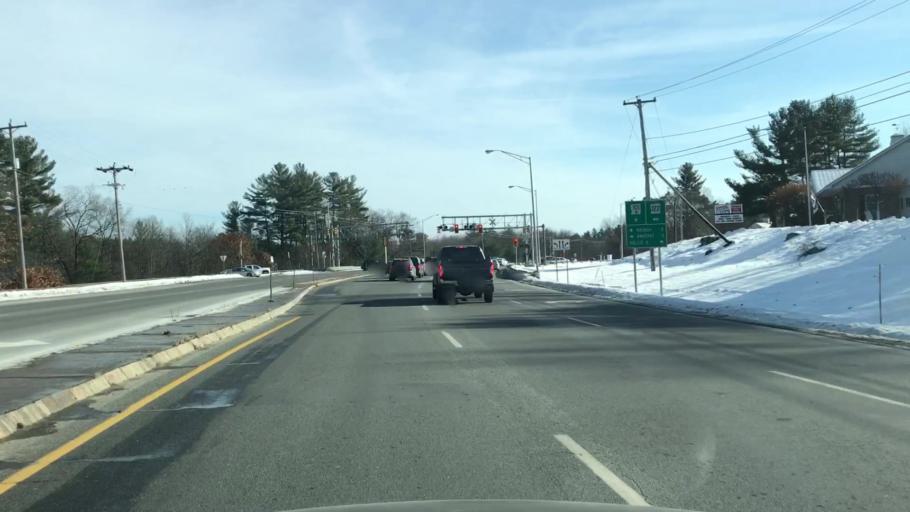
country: US
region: New Hampshire
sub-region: Hillsborough County
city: Milford
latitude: 42.8228
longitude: -71.6075
